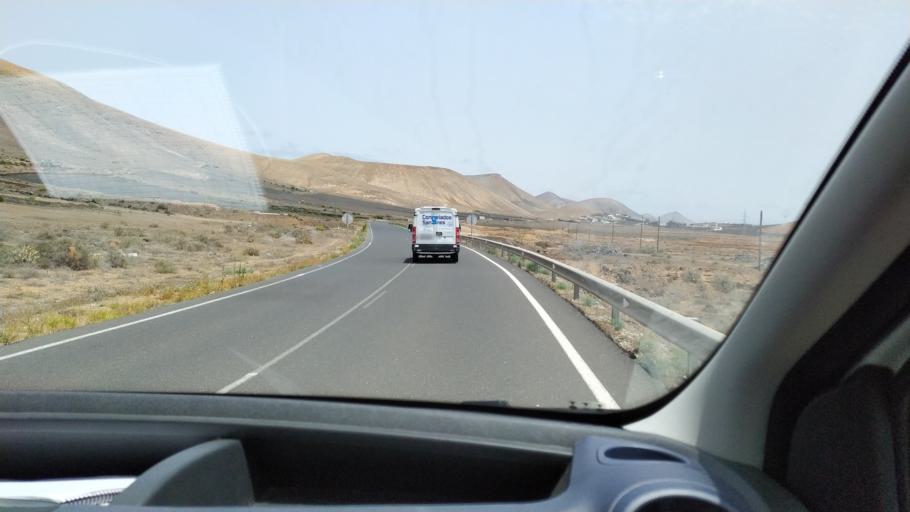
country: ES
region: Canary Islands
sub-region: Provincia de Las Palmas
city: Yaiza
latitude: 28.9231
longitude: -13.7662
